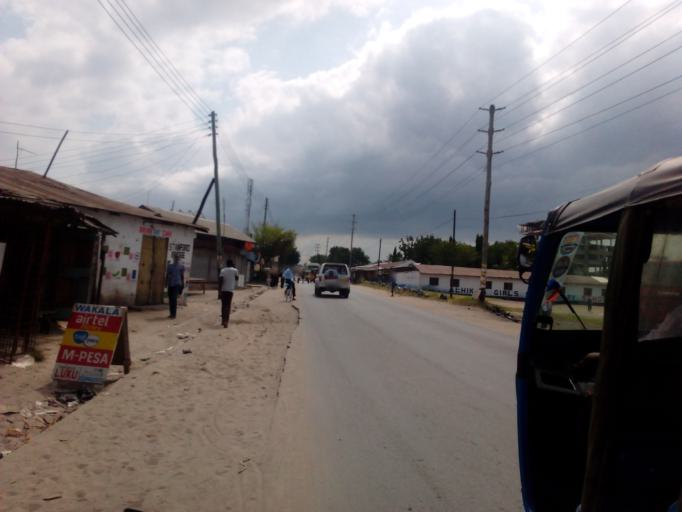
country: TZ
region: Dar es Salaam
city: Dar es Salaam
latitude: -6.8580
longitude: 39.2564
